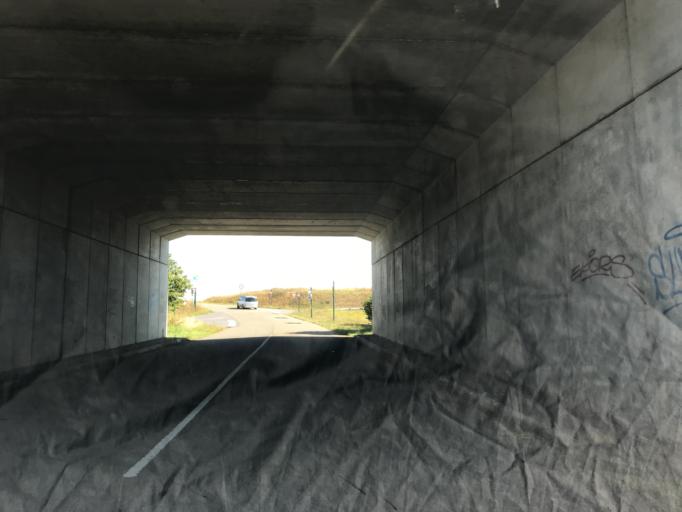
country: FR
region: Ile-de-France
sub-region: Departement du Val-d'Oise
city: Magny-en-Vexin
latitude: 49.1425
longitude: 1.8087
